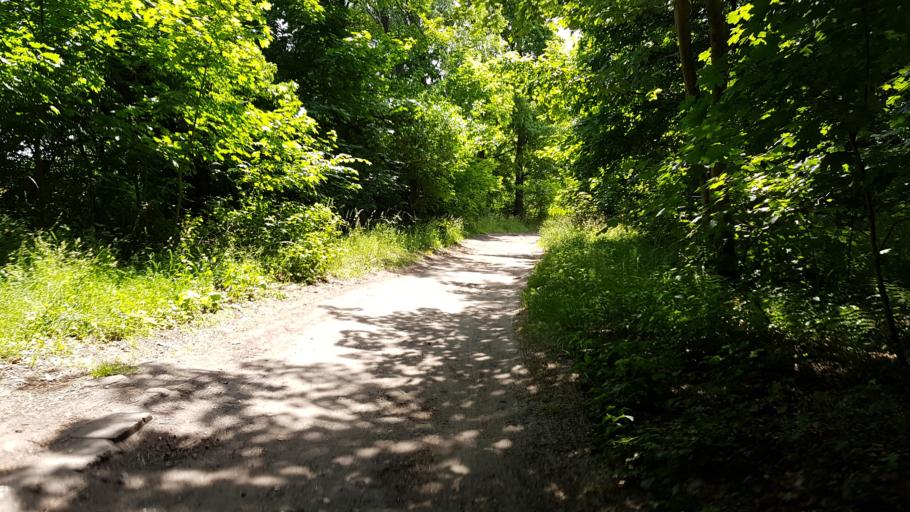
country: PL
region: West Pomeranian Voivodeship
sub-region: Swinoujscie
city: Swinoujscie
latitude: 53.9189
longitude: 14.2774
